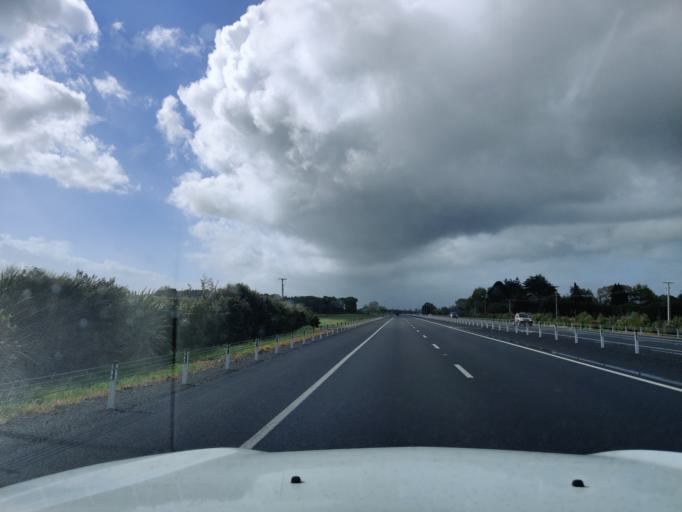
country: NZ
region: Waikato
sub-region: Waipa District
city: Cambridge
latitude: -37.8595
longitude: 175.3974
